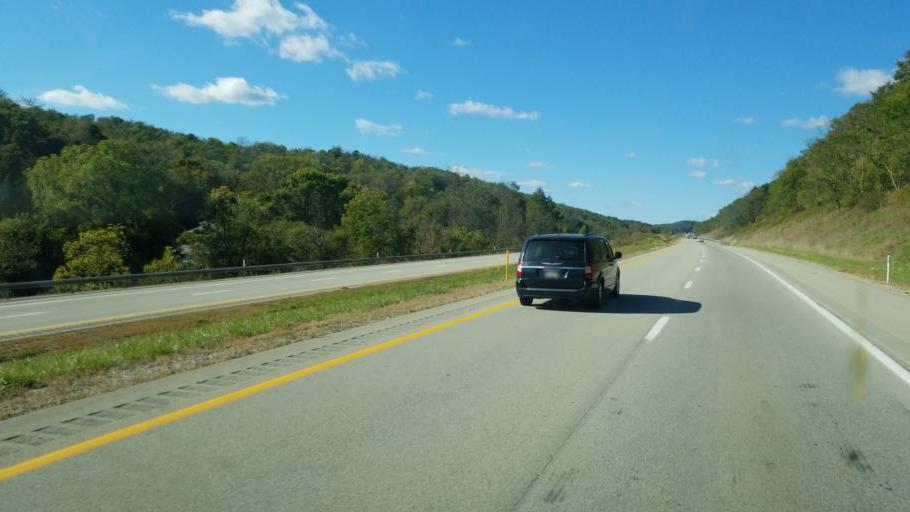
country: US
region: Pennsylvania
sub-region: Greene County
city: Waynesburg
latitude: 39.9674
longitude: -80.1740
